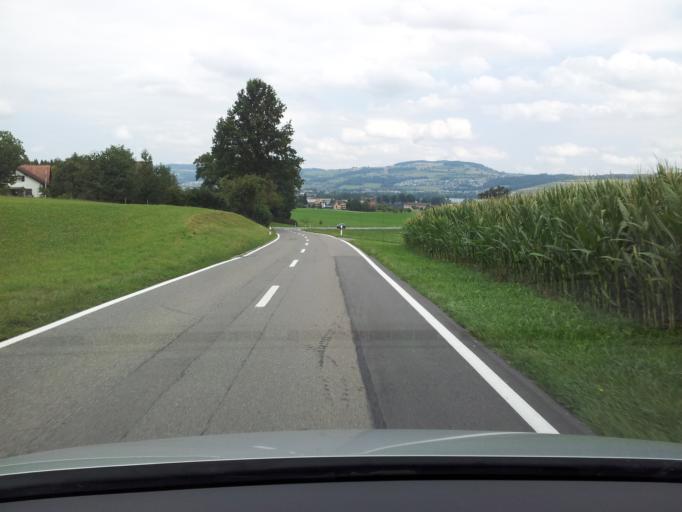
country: CH
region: Lucerne
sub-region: Sursee District
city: Oberkirch
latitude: 47.1413
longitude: 8.1143
